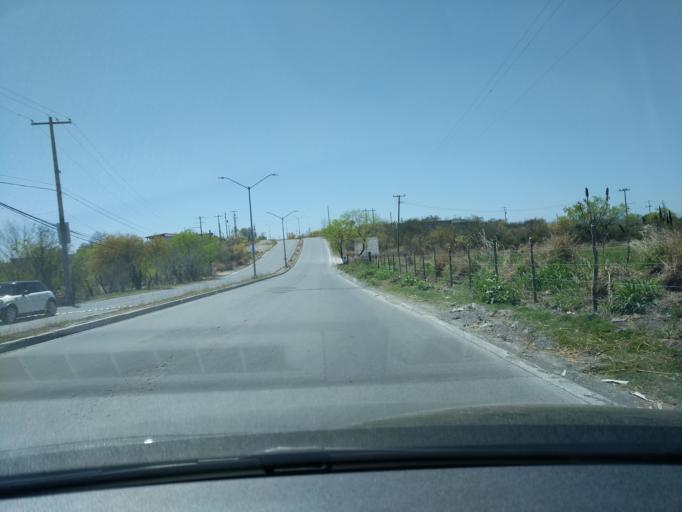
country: MX
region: Nuevo Leon
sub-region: Apodaca
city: Artemio Trevino
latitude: 25.8088
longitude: -100.1551
